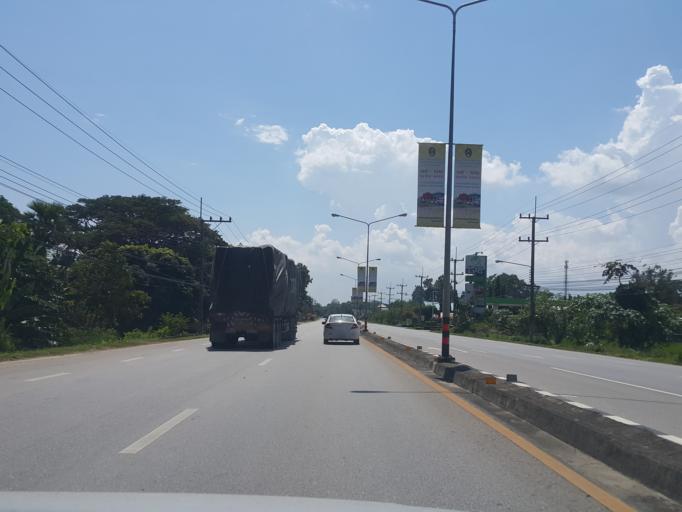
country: TH
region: Chiang Mai
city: Mae Taeng
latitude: 19.0090
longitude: 98.9445
